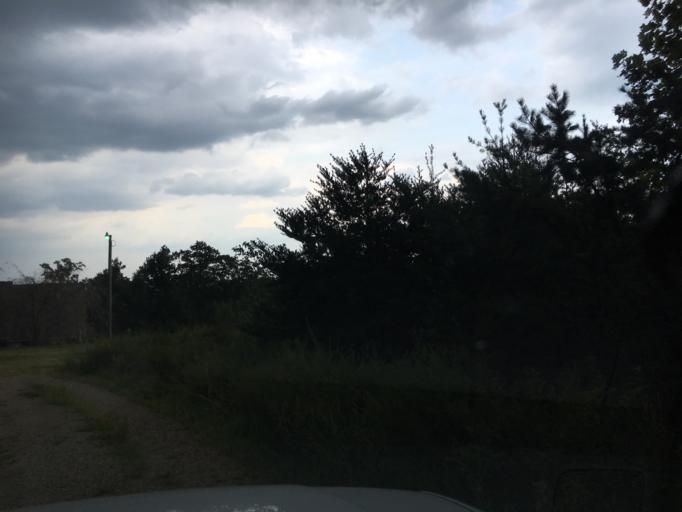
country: US
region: North Carolina
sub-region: Burke County
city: Glen Alpine
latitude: 35.7057
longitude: -81.8896
